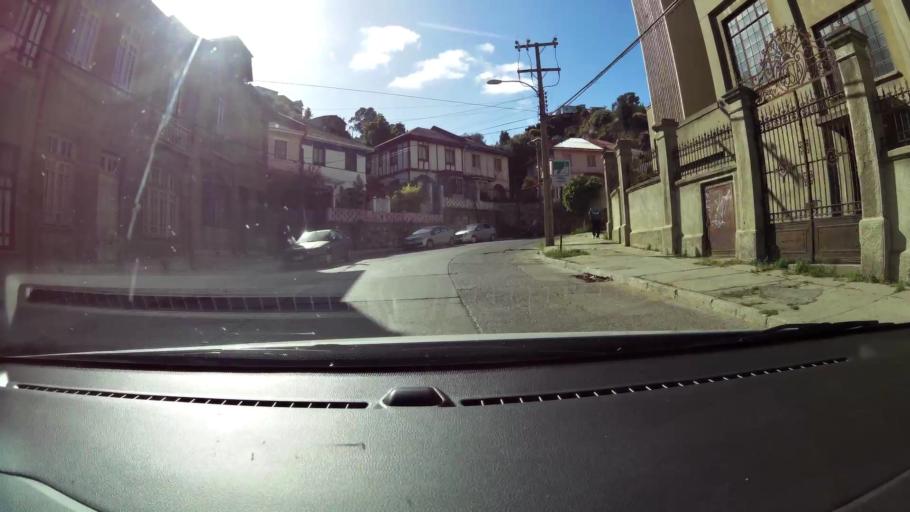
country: CL
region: Valparaiso
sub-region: Provincia de Valparaiso
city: Valparaiso
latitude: -33.0574
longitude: -71.6000
